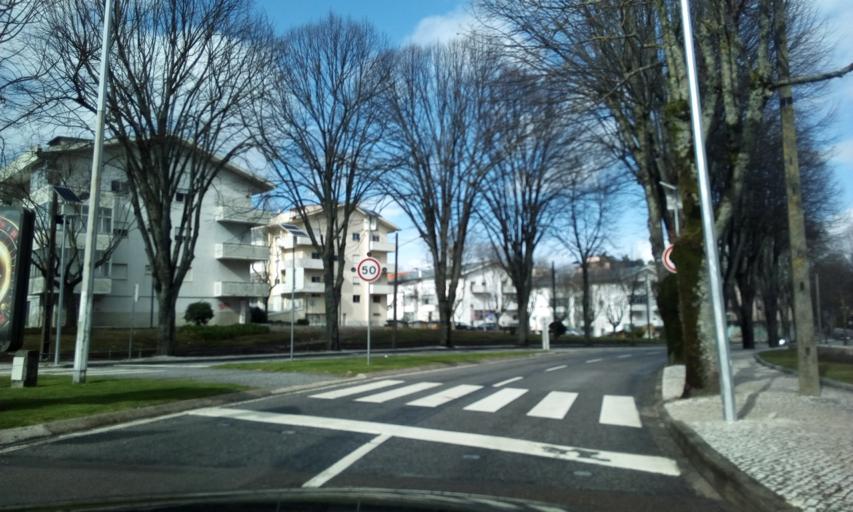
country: PT
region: Viseu
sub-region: Viseu
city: Viseu
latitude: 40.6493
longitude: -7.9119
